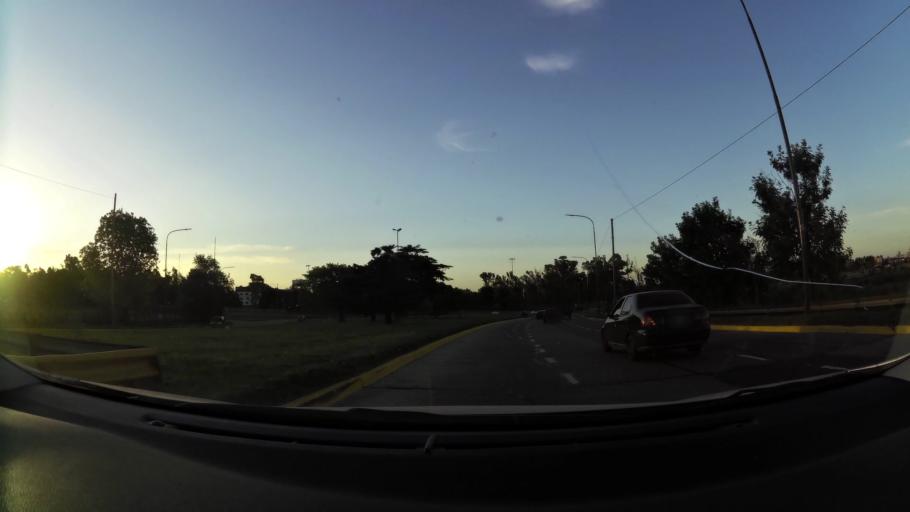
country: AR
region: Buenos Aires F.D.
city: Villa Lugano
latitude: -34.6705
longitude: -58.4624
